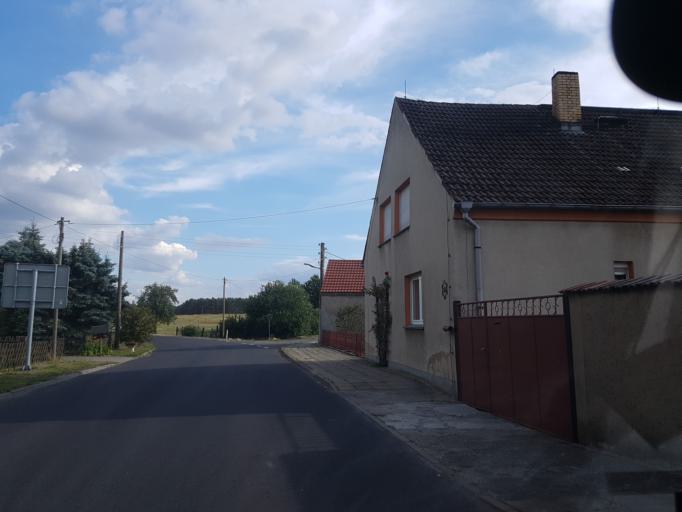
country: DE
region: Brandenburg
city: Herzberg
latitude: 51.7465
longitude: 13.2911
